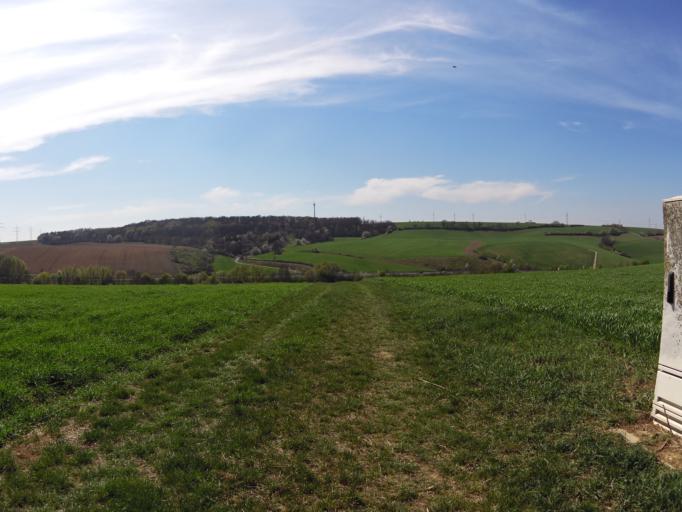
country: DE
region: Bavaria
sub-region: Regierungsbezirk Unterfranken
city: Rottendorf
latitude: 49.7870
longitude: 10.0431
